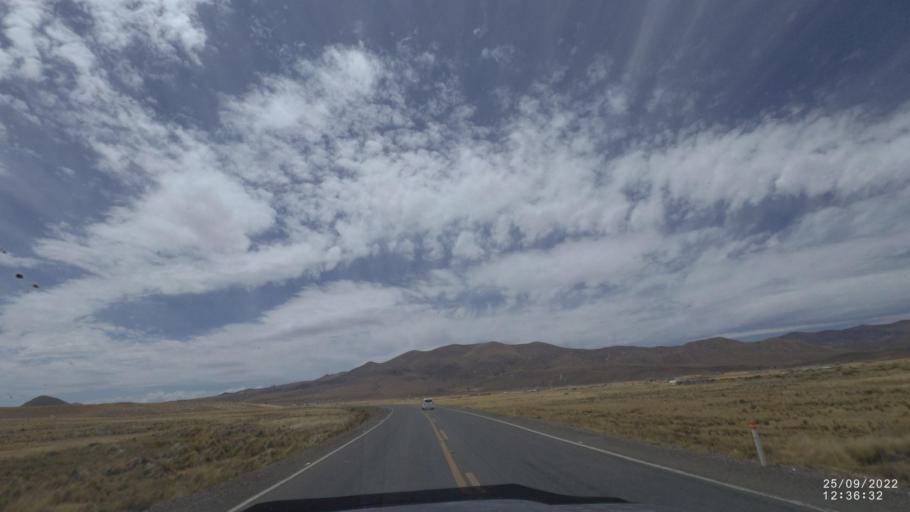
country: BO
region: Oruro
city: Machacamarca
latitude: -18.1629
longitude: -66.9878
